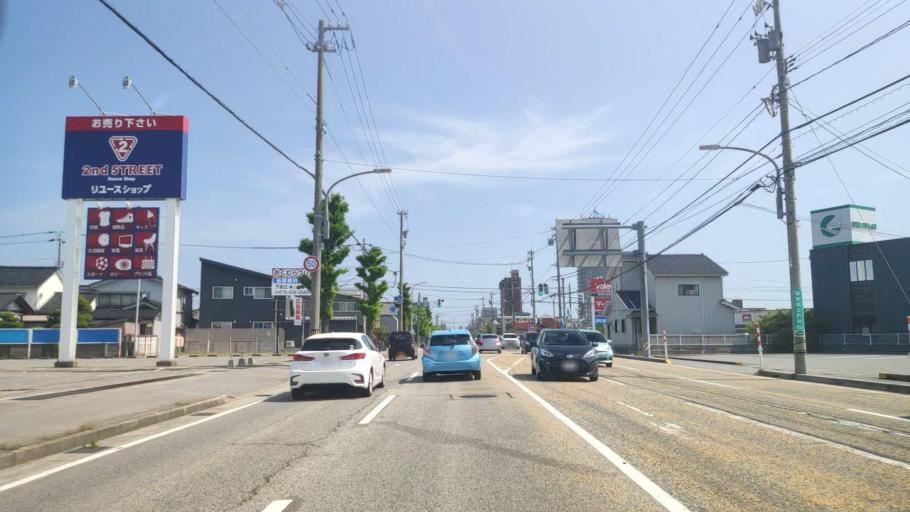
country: JP
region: Toyama
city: Toyama-shi
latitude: 36.7032
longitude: 137.2279
